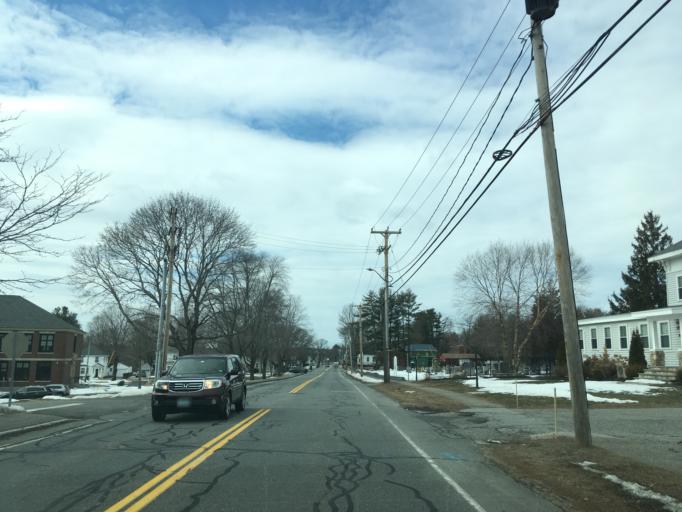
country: US
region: New Hampshire
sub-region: Rockingham County
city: Hampton
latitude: 42.9398
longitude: -70.8314
